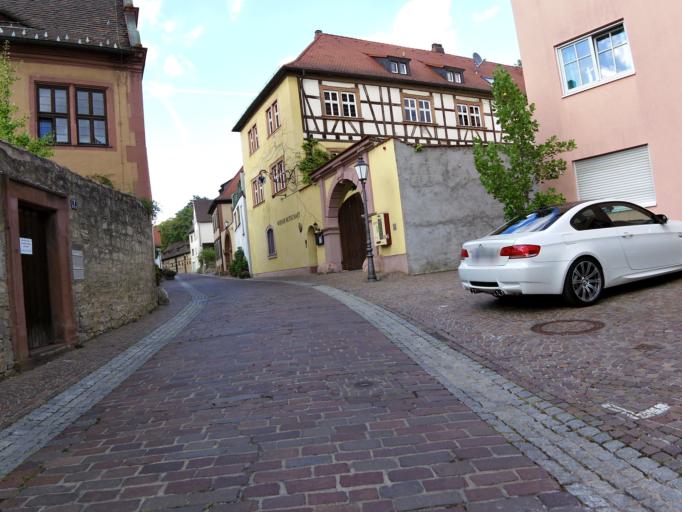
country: DE
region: Bavaria
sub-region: Regierungsbezirk Unterfranken
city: Veitshochheim
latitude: 49.8334
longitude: 9.8746
